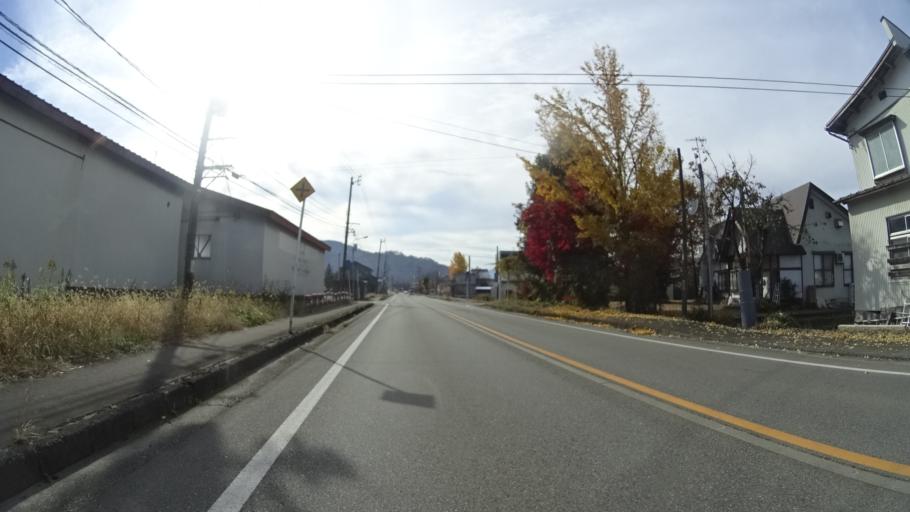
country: JP
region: Niigata
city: Muikamachi
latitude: 37.0907
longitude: 138.9146
